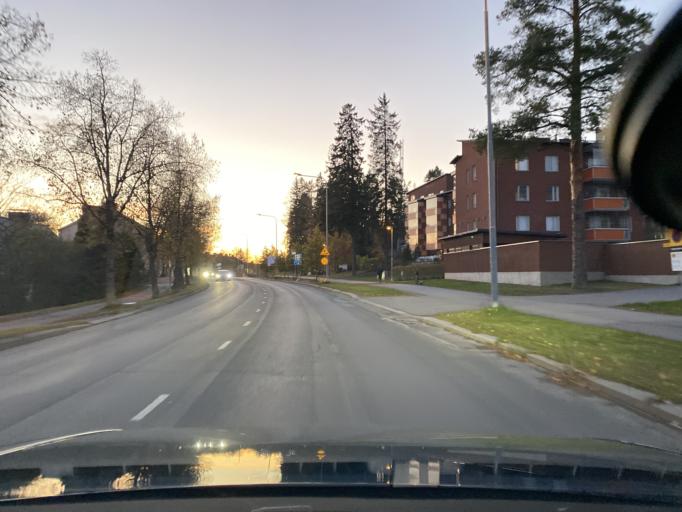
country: FI
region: Pirkanmaa
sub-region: Tampere
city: Tampere
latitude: 61.4703
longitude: 23.7440
